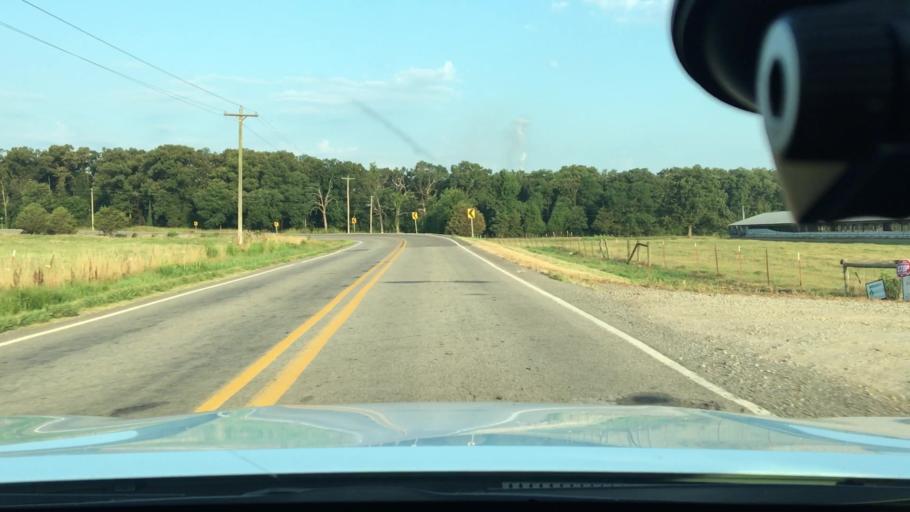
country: US
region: Arkansas
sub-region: Johnson County
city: Coal Hill
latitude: 35.3794
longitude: -93.5586
